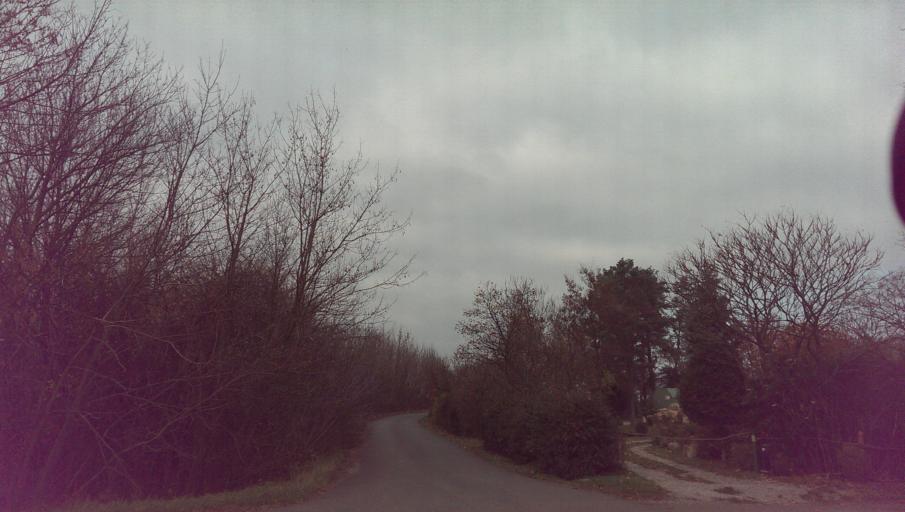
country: CZ
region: Zlin
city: Tlumacov
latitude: 49.2691
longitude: 17.4922
